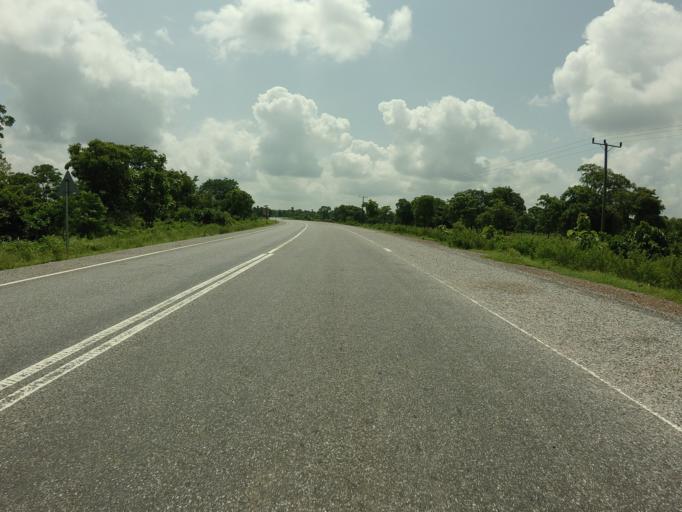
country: GH
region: Northern
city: Tamale
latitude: 9.1313
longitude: -1.5955
